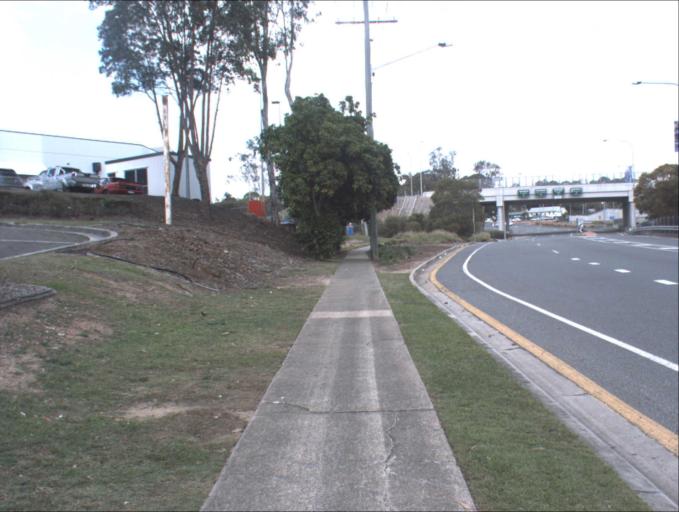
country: AU
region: Queensland
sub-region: Logan
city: Park Ridge South
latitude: -27.6970
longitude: 153.0381
